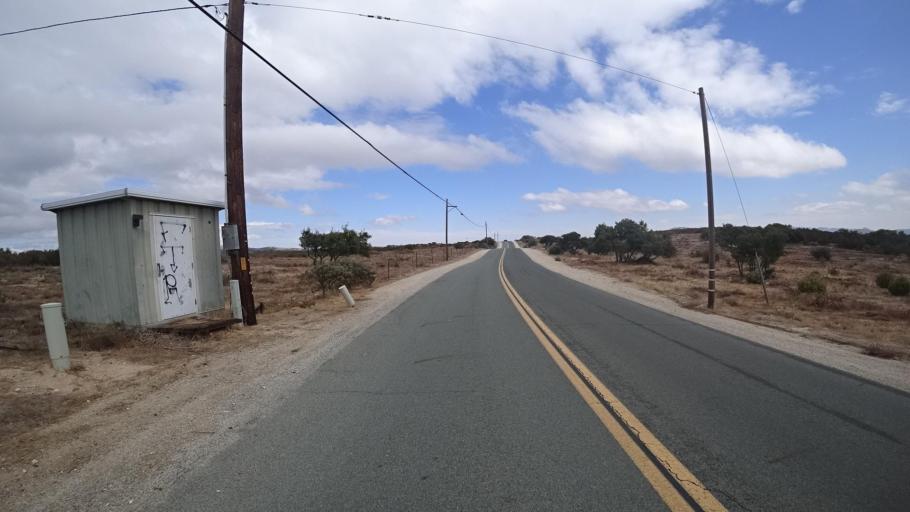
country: US
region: California
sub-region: San Diego County
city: Campo
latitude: 32.6510
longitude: -116.3168
